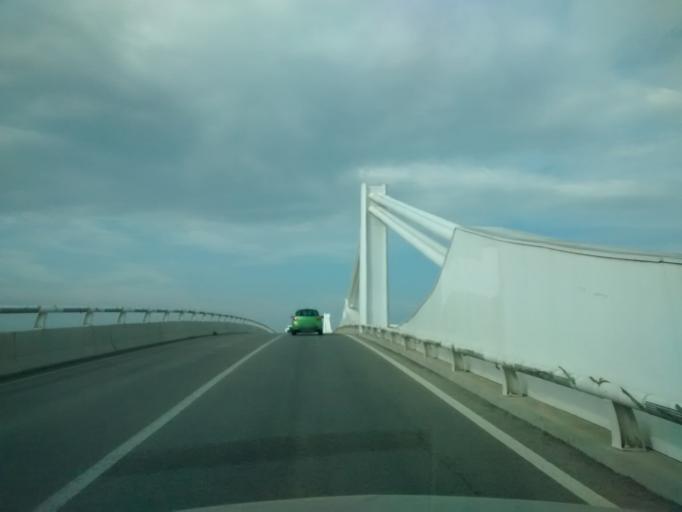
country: ES
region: Catalonia
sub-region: Provincia de Tarragona
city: Deltebre
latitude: 40.7122
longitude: 0.7171
